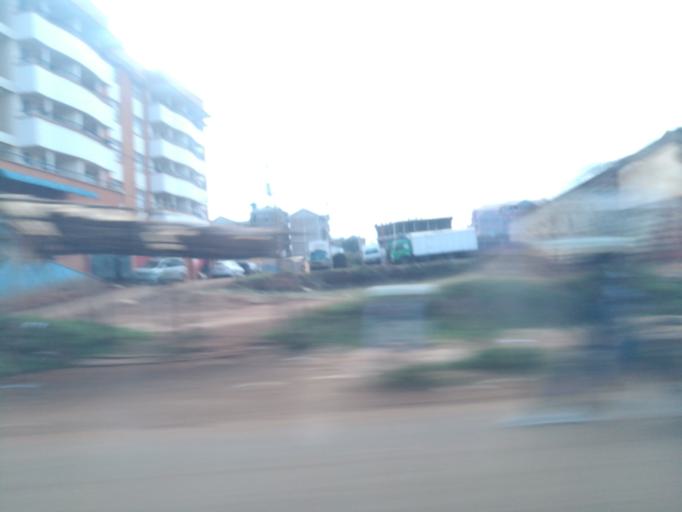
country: KE
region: Nairobi Area
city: Thika
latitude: -1.1080
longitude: 37.0141
